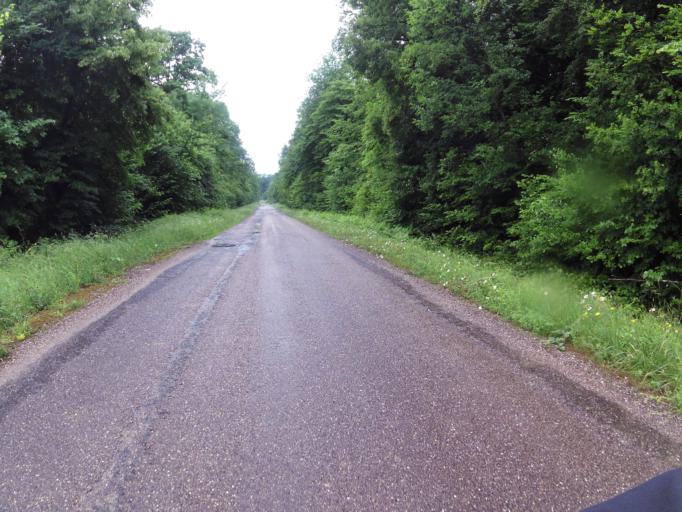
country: FR
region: Champagne-Ardenne
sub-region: Departement de la Marne
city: Sermaize-les-Bains
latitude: 48.7647
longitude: 4.9441
